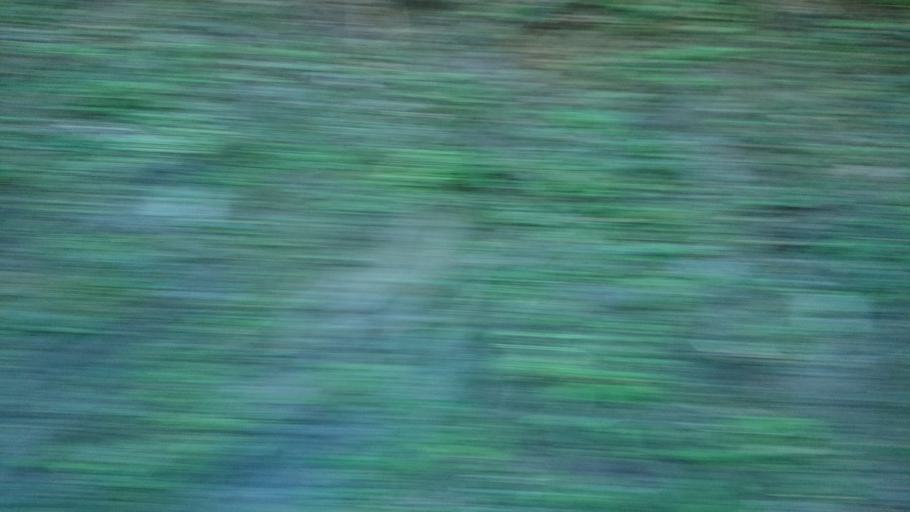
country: TW
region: Taiwan
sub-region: Yilan
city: Yilan
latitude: 24.5784
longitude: 121.4877
